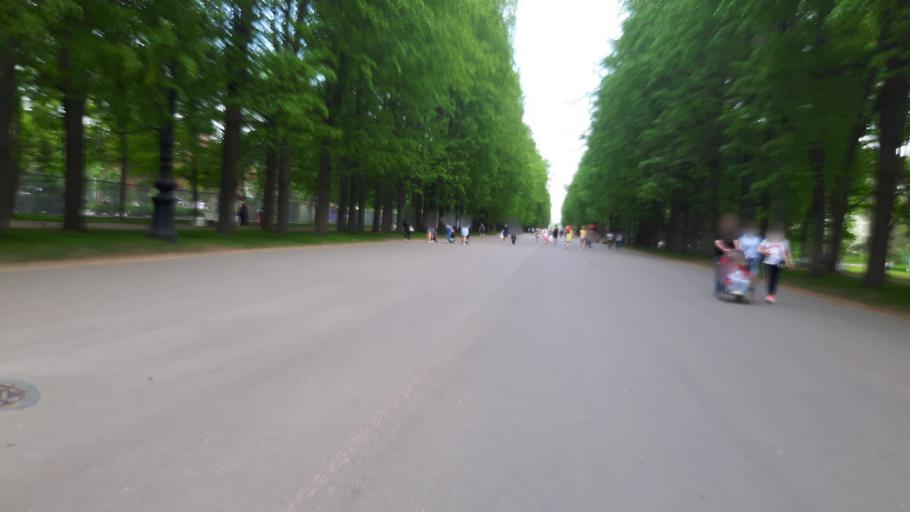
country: RU
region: Leningrad
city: Krestovskiy ostrov
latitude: 59.9719
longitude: 30.2445
